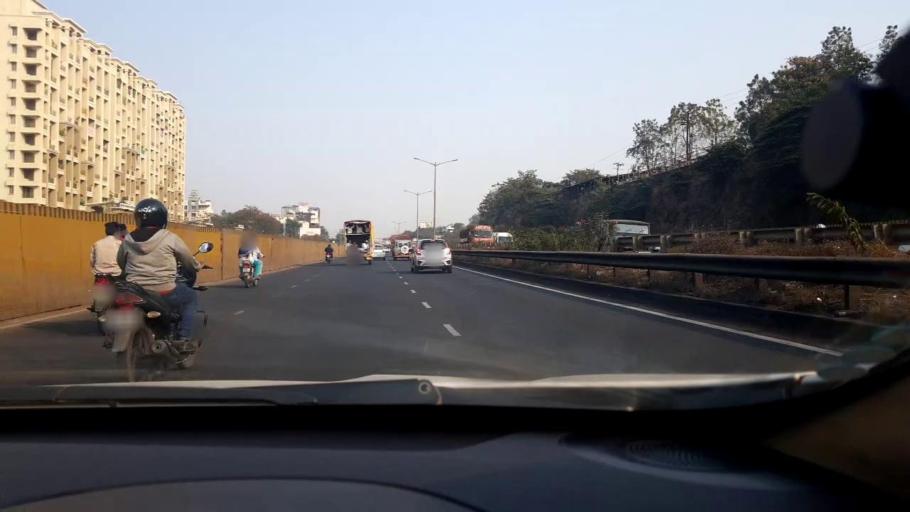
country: IN
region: Maharashtra
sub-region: Pune Division
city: Kharakvasla
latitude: 18.5086
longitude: 73.7780
